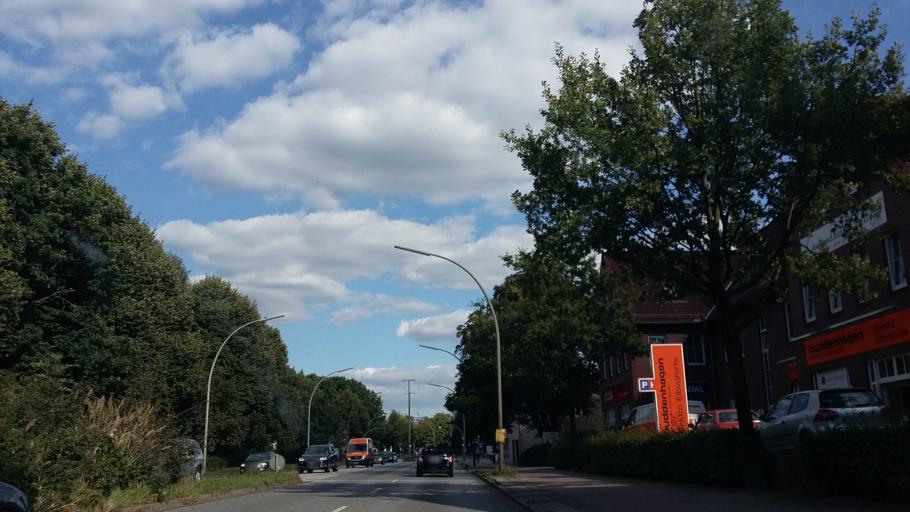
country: DE
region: Schleswig-Holstein
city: Halstenbek
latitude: 53.5733
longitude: 9.8407
